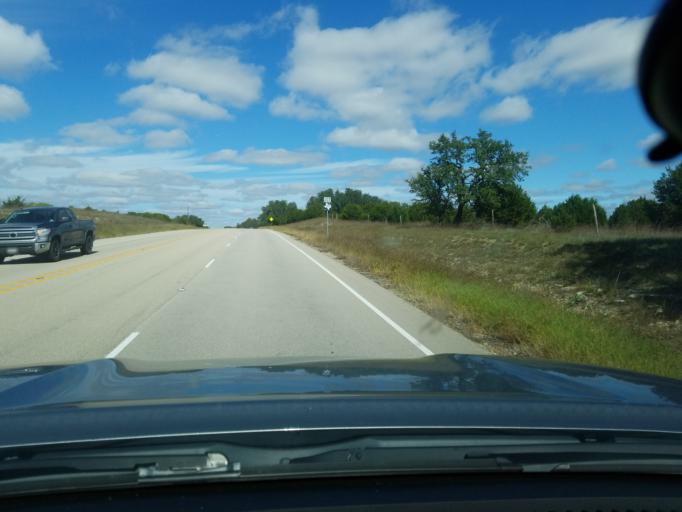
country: US
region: Texas
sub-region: Hamilton County
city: Hamilton
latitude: 31.5877
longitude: -98.1567
